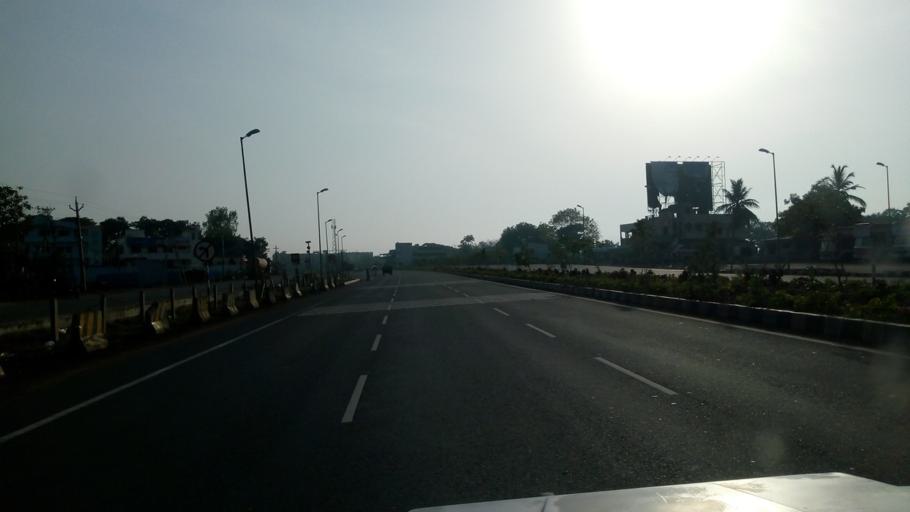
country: IN
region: Andhra Pradesh
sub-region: Guntur
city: Mangalagiri
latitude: 16.3973
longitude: 80.5476
